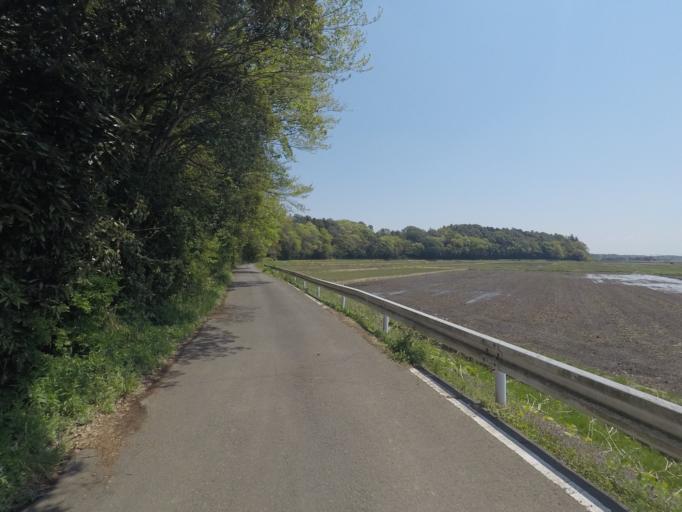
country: JP
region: Ibaraki
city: Ushiku
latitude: 36.0004
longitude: 140.0991
